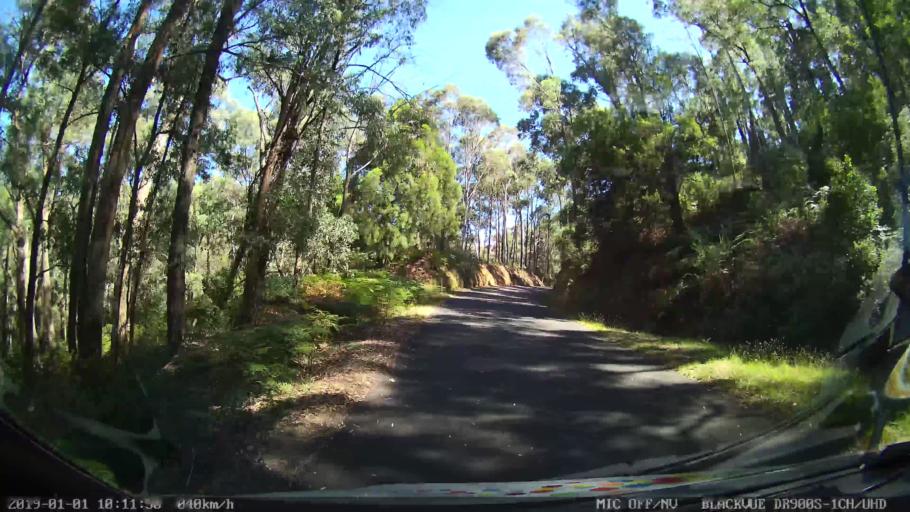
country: AU
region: New South Wales
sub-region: Snowy River
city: Jindabyne
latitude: -36.1349
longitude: 148.1563
